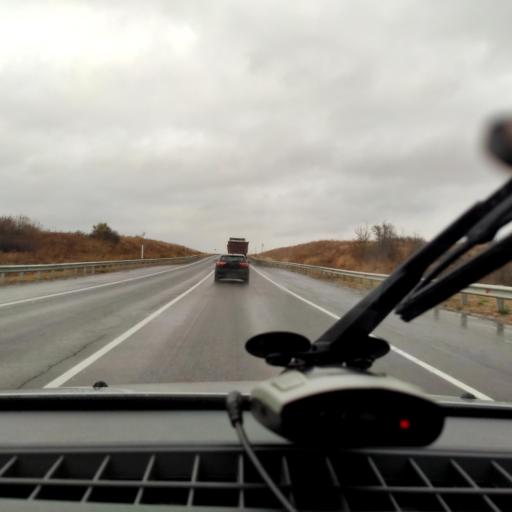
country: RU
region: Voronezj
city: Strelitsa
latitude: 51.5203
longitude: 38.9680
